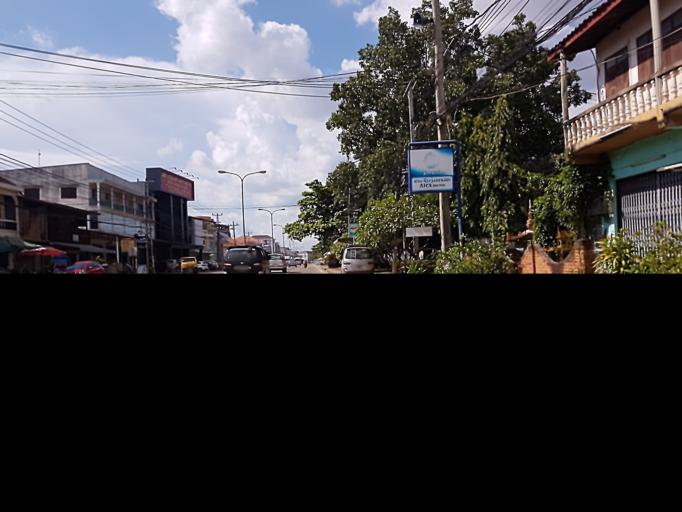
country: TH
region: Nong Khai
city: Si Chiang Mai
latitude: 17.9221
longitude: 102.6181
